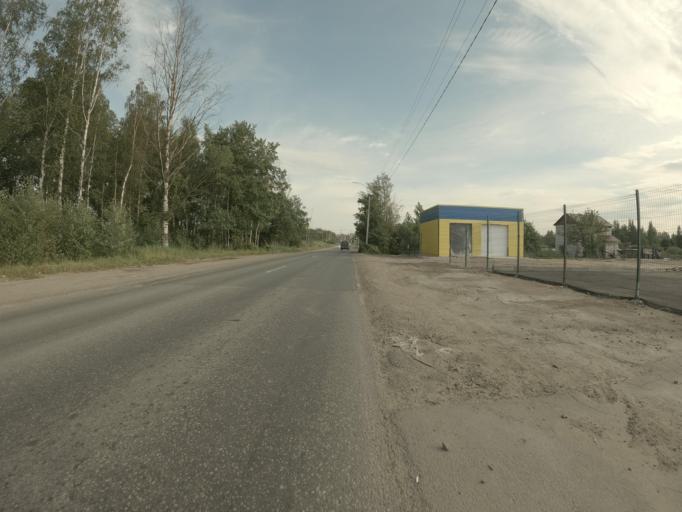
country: RU
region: St.-Petersburg
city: Krasnogvargeisky
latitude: 59.9341
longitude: 30.5204
